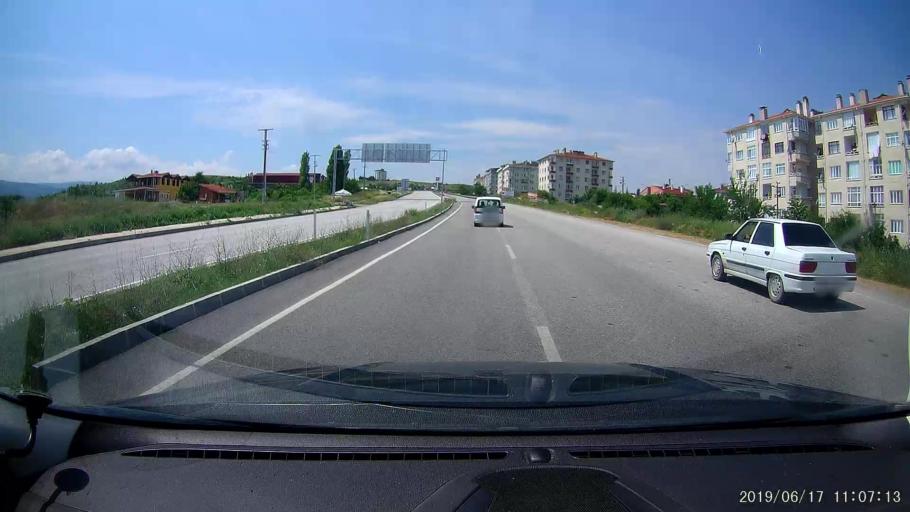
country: TR
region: Kastamonu
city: Tosya
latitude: 41.0056
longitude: 34.0567
